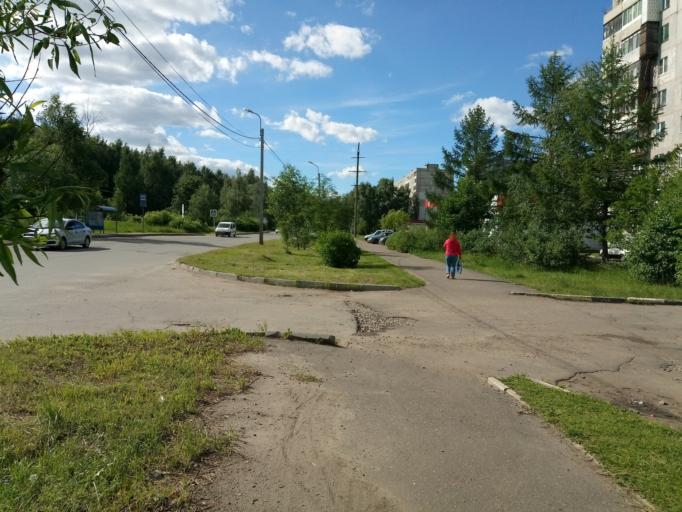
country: RU
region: Jaroslavl
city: Yaroslavl
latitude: 57.6420
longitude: 39.9450
